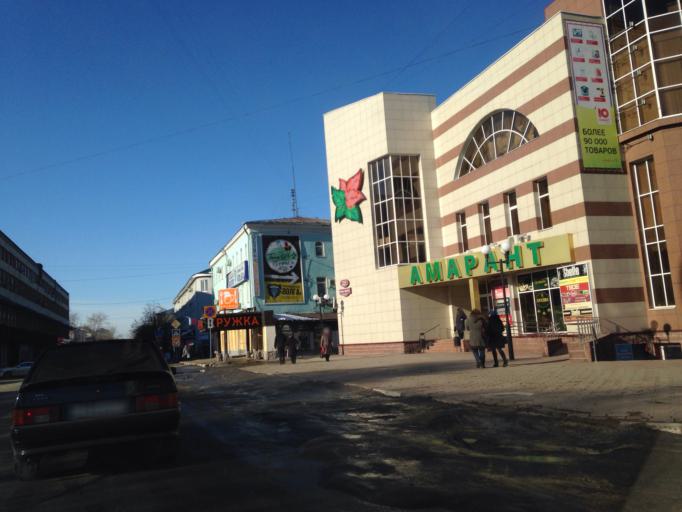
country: RU
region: Ulyanovsk
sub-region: Ulyanovskiy Rayon
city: Ulyanovsk
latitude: 54.3194
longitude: 48.3960
